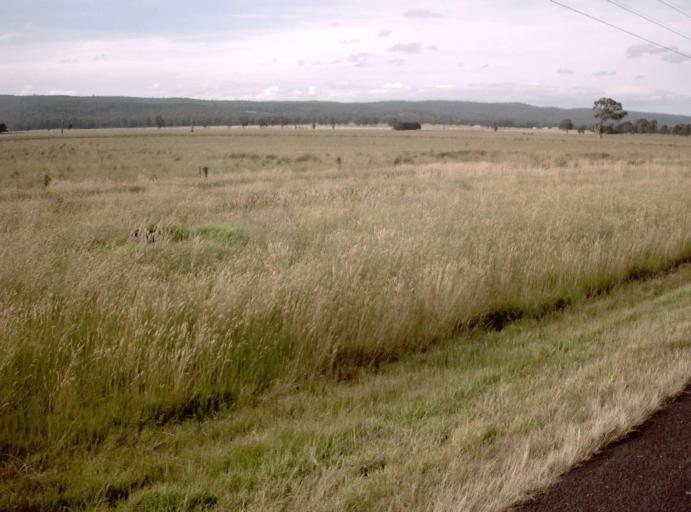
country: AU
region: Victoria
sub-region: Latrobe
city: Traralgon
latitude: -38.0894
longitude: 146.6022
